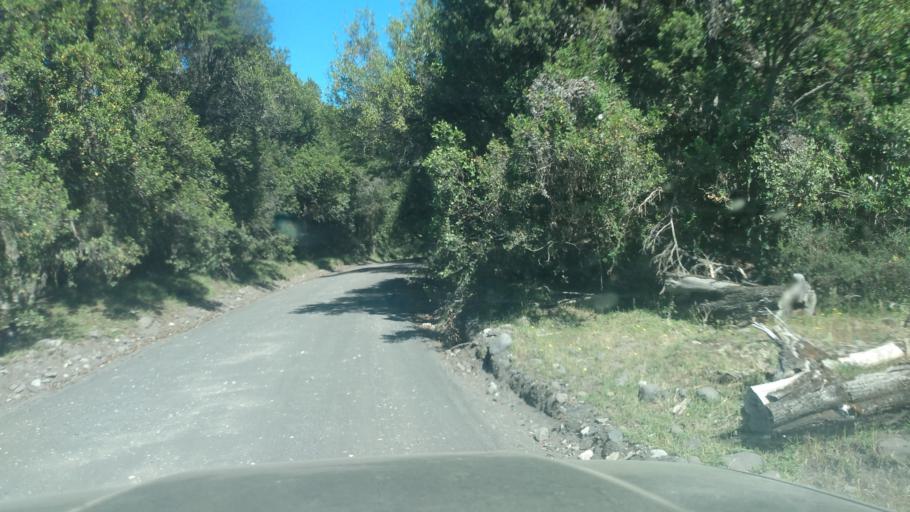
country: AR
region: Neuquen
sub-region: Departamento de Lacar
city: San Martin de los Andes
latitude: -39.7477
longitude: -71.5014
